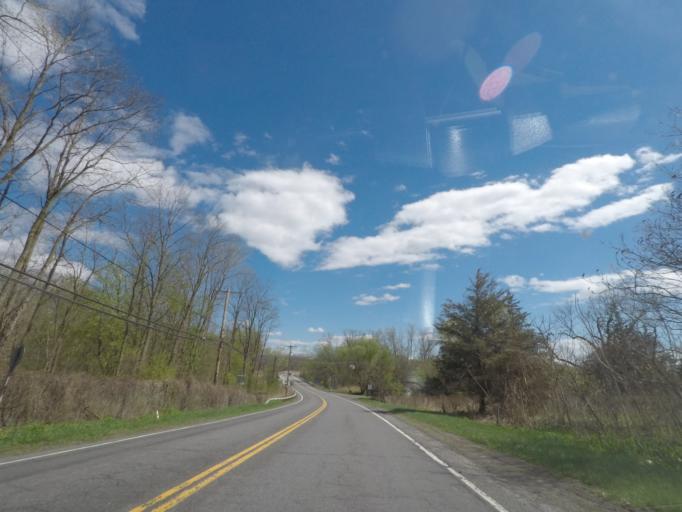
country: US
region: New York
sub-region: Columbia County
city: Oakdale
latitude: 42.2384
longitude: -73.7582
